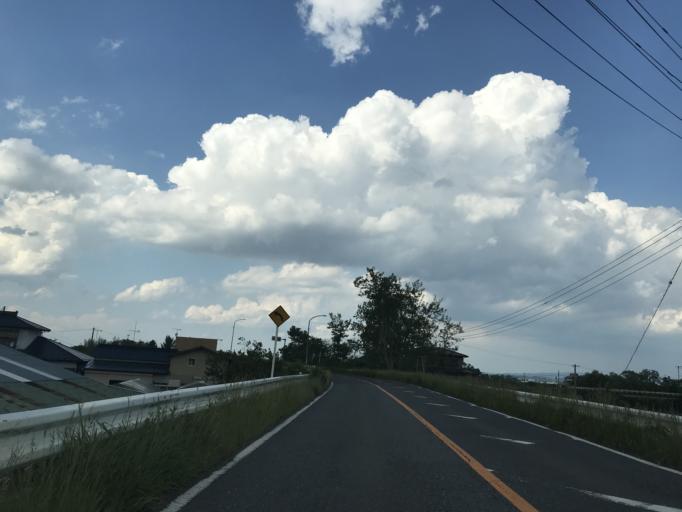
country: JP
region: Miyagi
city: Wakuya
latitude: 38.5965
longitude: 141.1678
